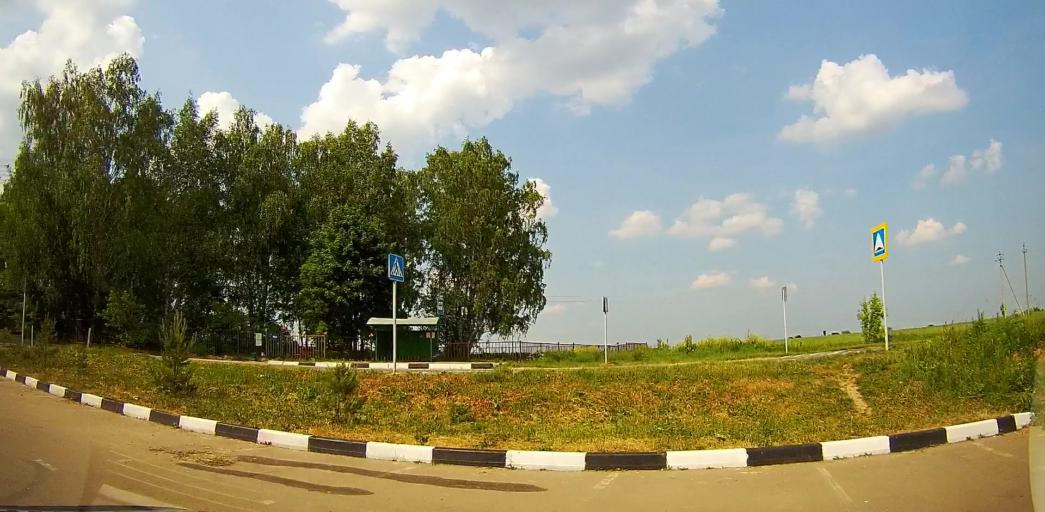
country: RU
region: Moskovskaya
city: Zhilevo
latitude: 55.0549
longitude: 38.0528
